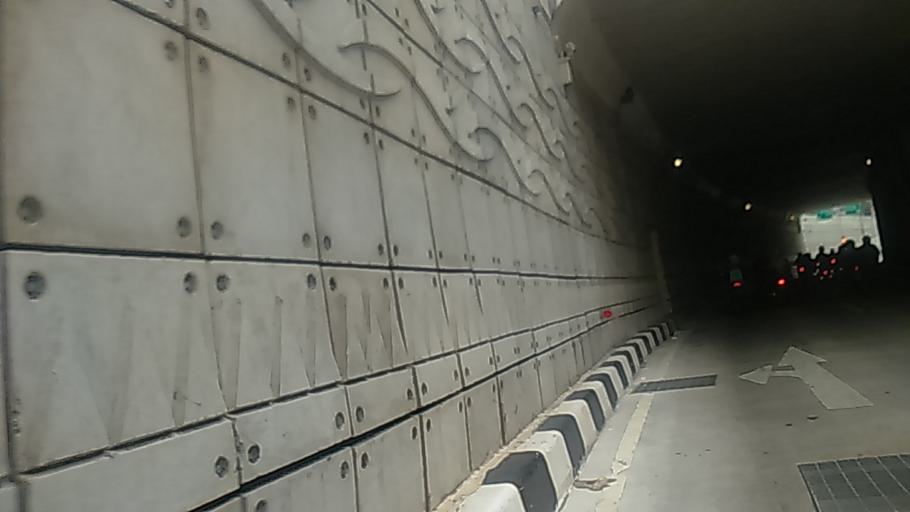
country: ID
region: Jakarta Raya
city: Jakarta
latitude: -6.2420
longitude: 106.8257
